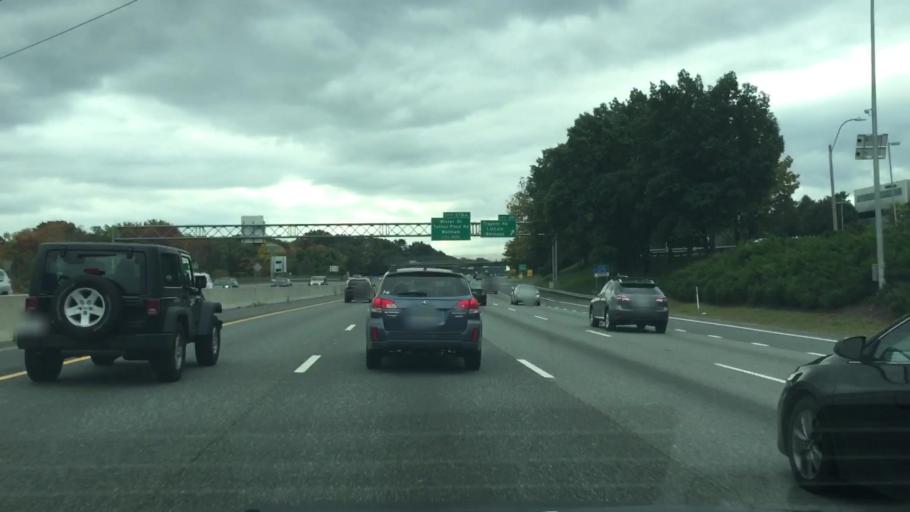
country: US
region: Massachusetts
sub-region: Middlesex County
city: Lexington
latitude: 42.4187
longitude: -71.2570
